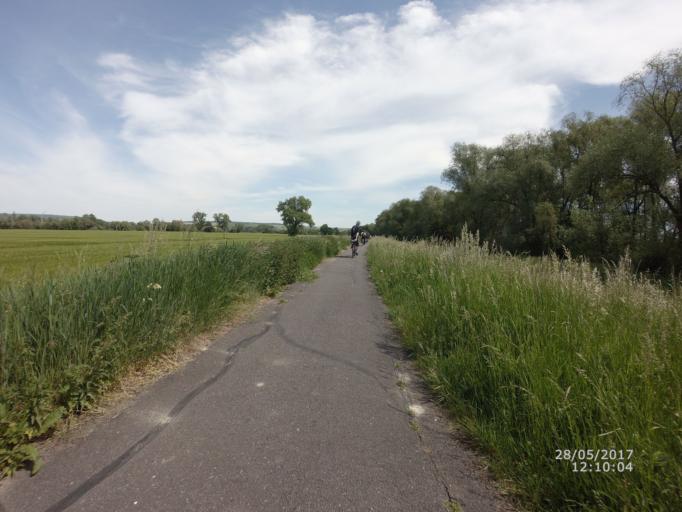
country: DE
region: Thuringia
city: Etzleben
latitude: 51.2568
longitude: 11.1650
